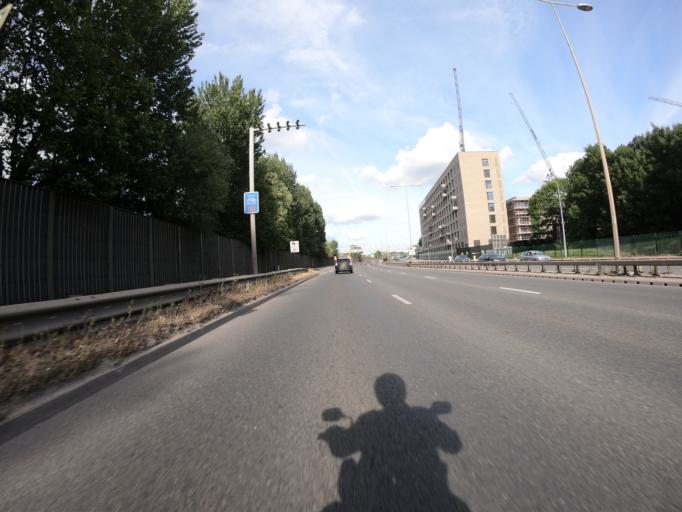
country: GB
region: England
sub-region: Greater London
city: East Ham
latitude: 51.5202
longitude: 0.0446
